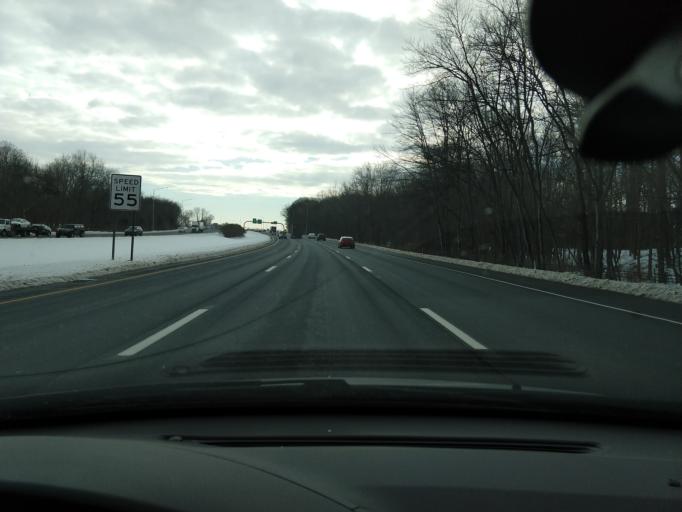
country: US
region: Connecticut
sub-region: New Haven County
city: Wolcott
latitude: 41.5917
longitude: -72.9030
